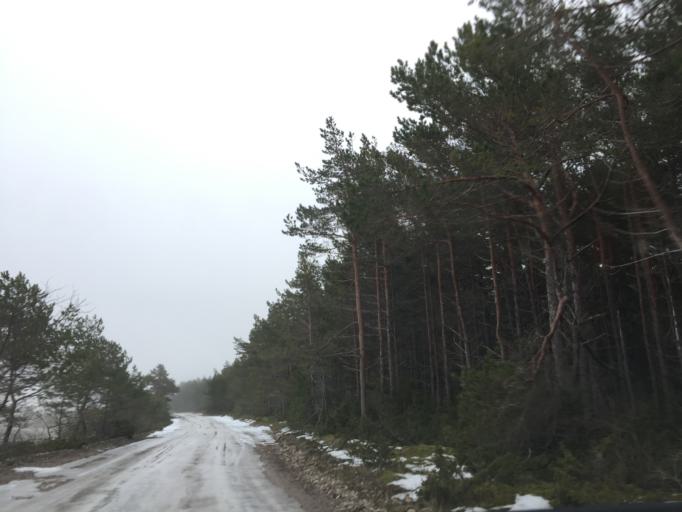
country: EE
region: Saare
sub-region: Kuressaare linn
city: Kuressaare
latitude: 58.5110
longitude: 21.9452
